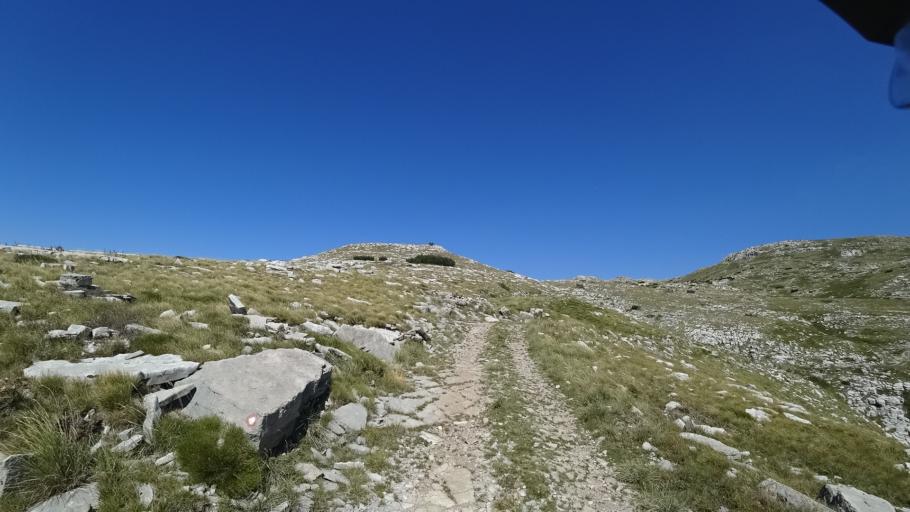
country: HR
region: Splitsko-Dalmatinska
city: Hrvace
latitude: 43.9277
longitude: 16.6024
